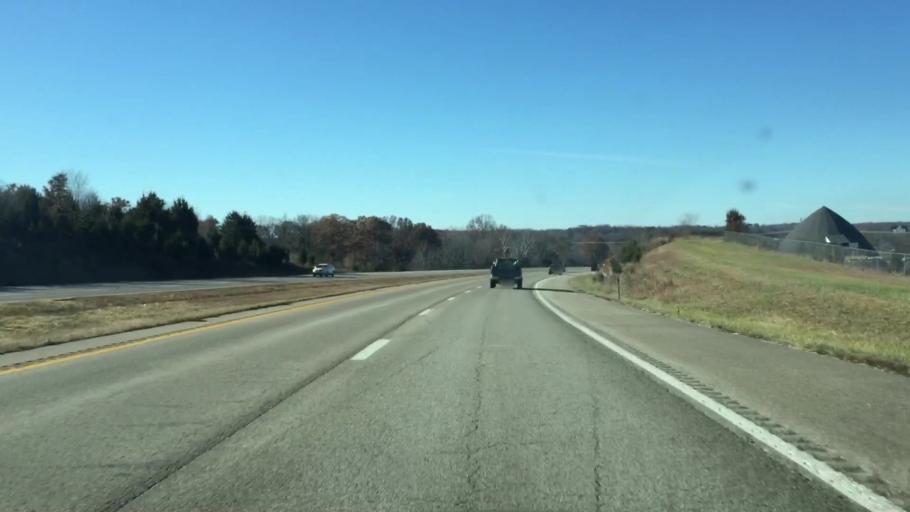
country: US
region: Missouri
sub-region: Cole County
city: Wardsville
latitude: 38.5104
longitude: -92.2453
